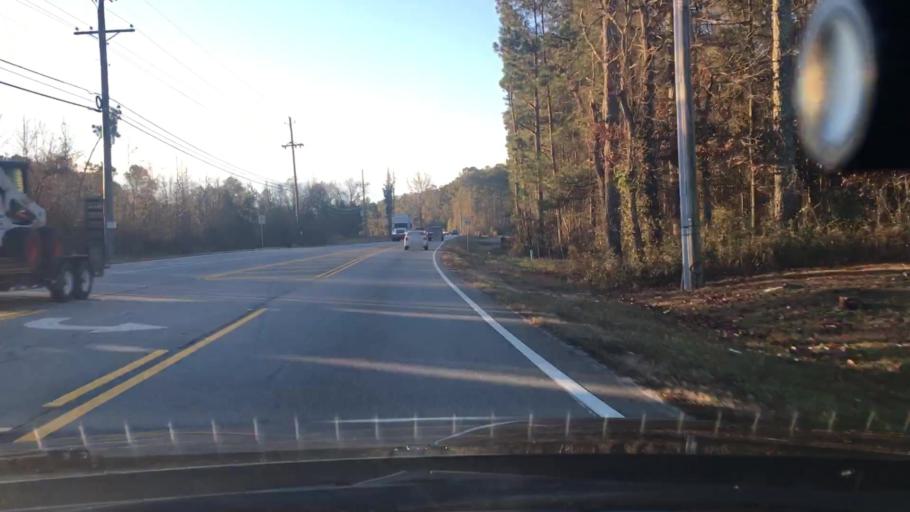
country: US
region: Georgia
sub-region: Fayette County
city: Peachtree City
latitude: 33.4062
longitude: -84.6822
